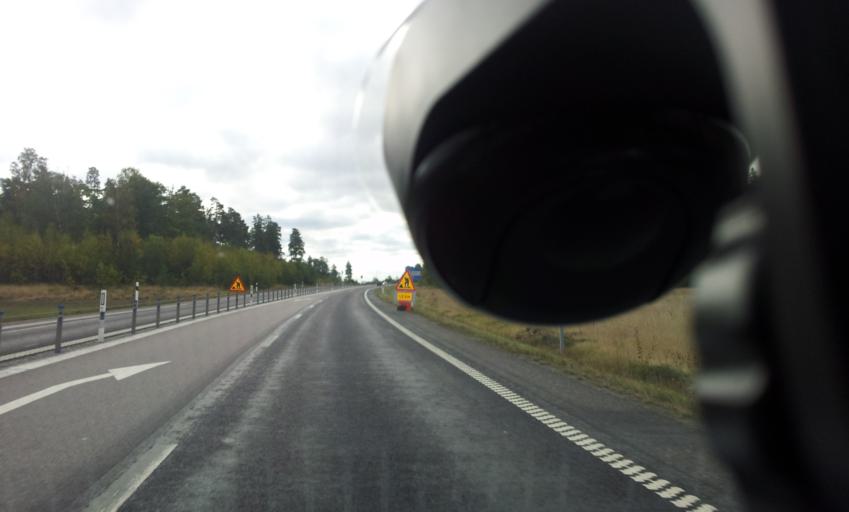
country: SE
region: OEstergoetland
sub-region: Soderkopings Kommun
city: Soederkoeping
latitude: 58.5014
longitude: 16.3008
